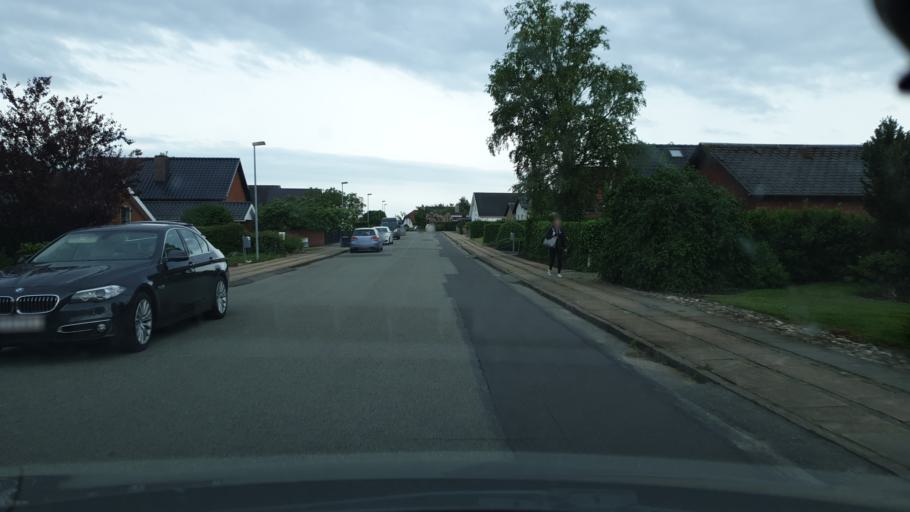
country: DK
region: South Denmark
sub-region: Kolding Kommune
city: Kolding
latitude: 55.5011
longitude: 9.4947
